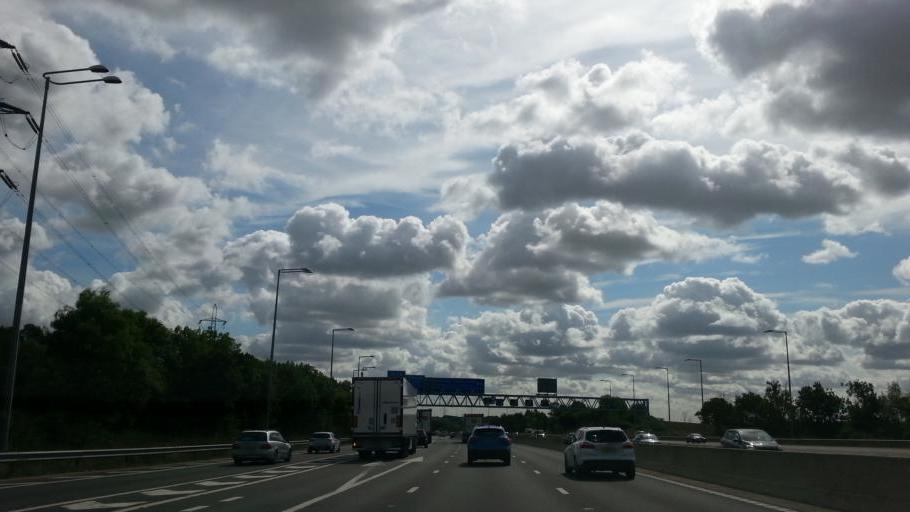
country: GB
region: England
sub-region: Essex
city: Epping
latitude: 51.6818
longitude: 0.1127
